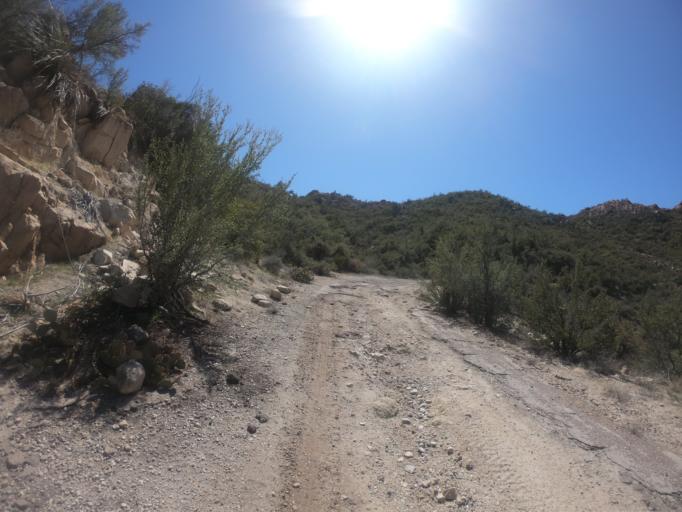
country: US
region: Arizona
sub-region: Gila County
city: Miami
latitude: 33.3559
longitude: -110.9562
